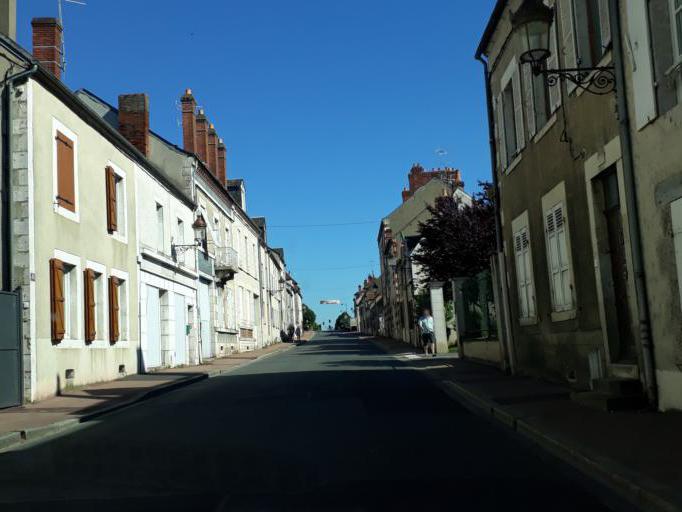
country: FR
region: Centre
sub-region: Departement du Loiret
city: Briare
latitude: 47.6373
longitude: 2.7403
